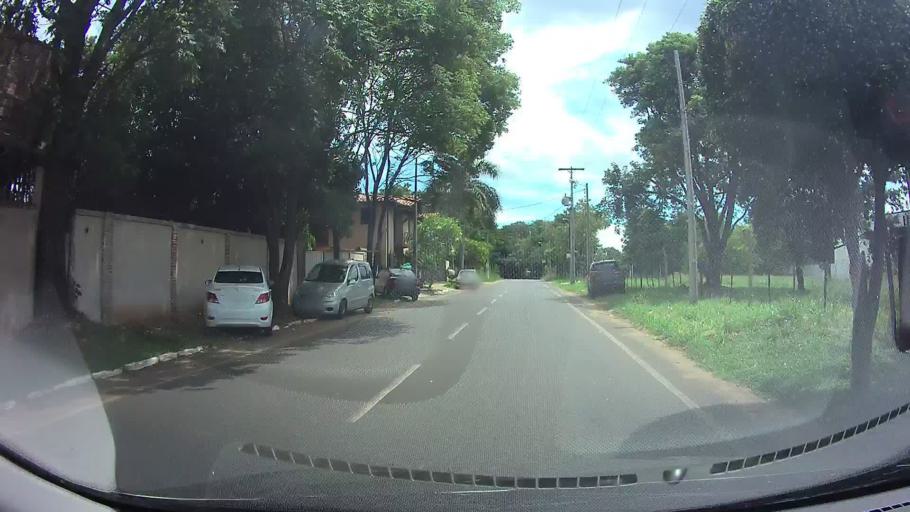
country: PY
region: Central
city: Fernando de la Mora
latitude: -25.3202
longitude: -57.5298
